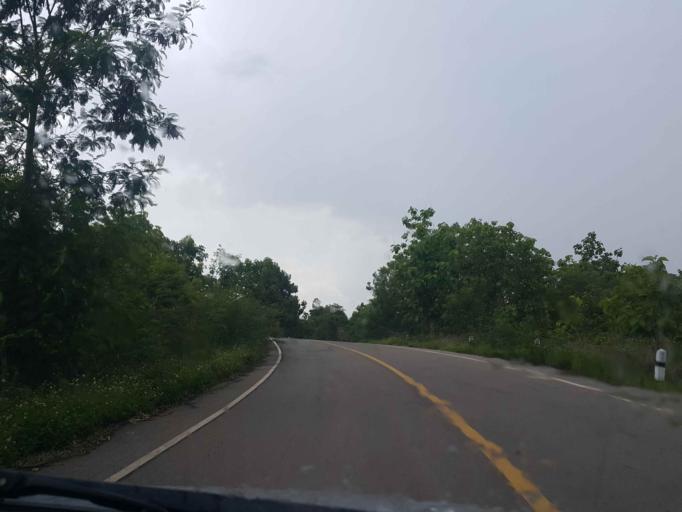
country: TH
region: Phayao
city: Dok Kham Tai
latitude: 19.0318
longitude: 99.9601
